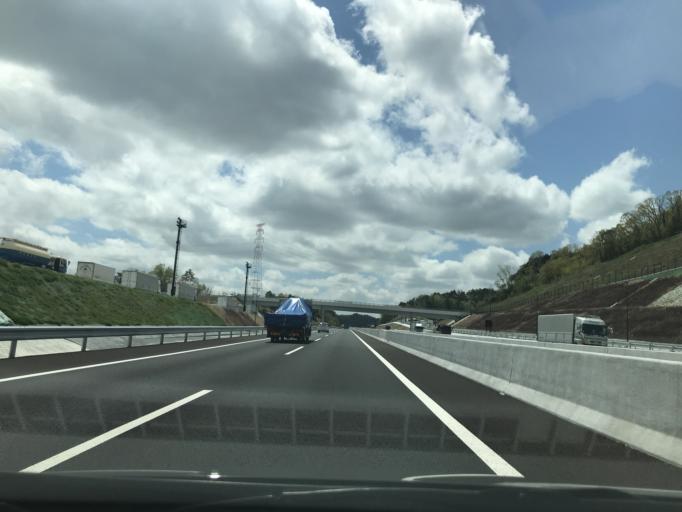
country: JP
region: Osaka
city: Ibaraki
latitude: 34.8833
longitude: 135.5334
